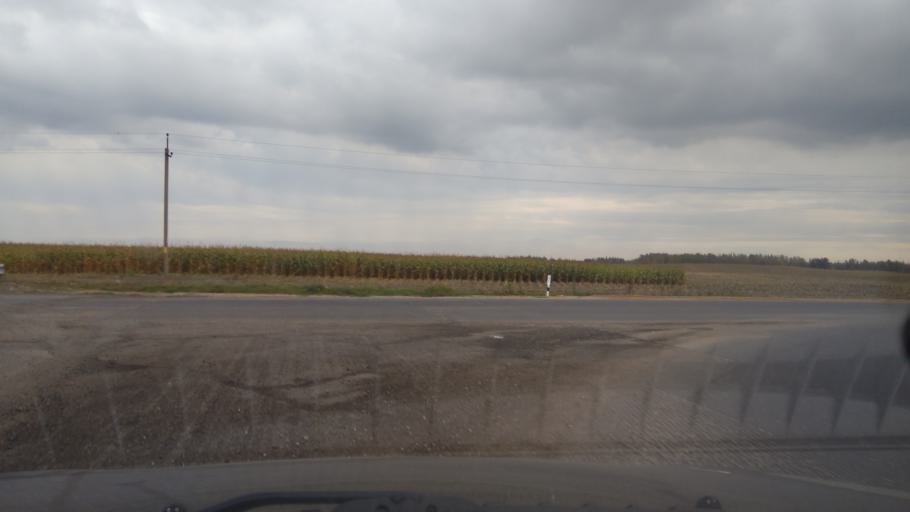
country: BY
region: Minsk
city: Dukora
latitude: 53.6553
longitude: 27.9444
